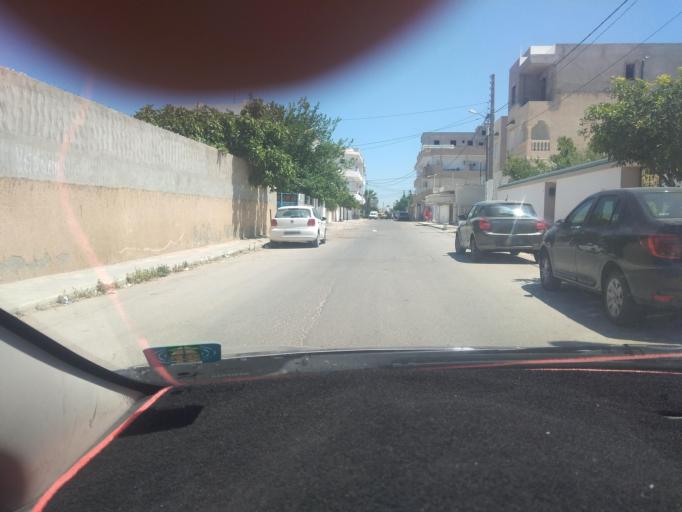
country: TN
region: Susah
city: Hammam Sousse
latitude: 35.8501
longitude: 10.5926
